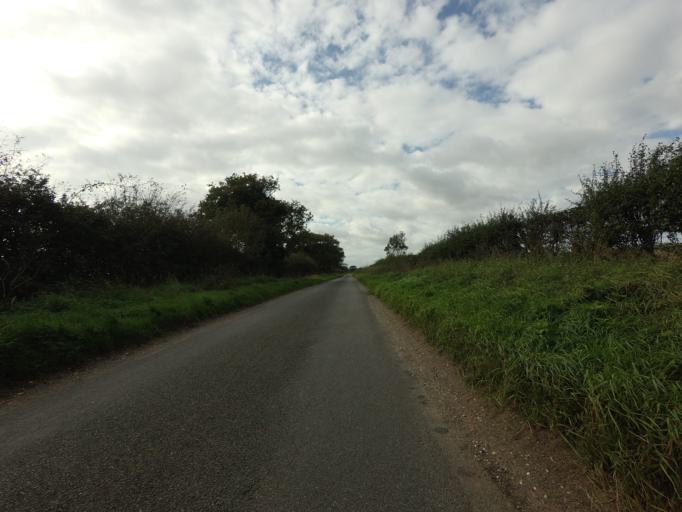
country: GB
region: England
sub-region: Norfolk
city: Hunstanton
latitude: 52.9341
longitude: 0.5536
